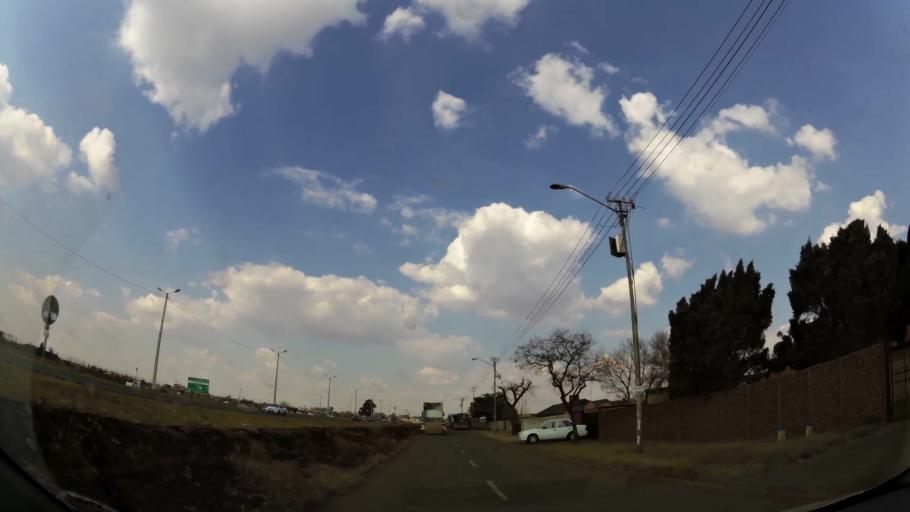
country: ZA
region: Gauteng
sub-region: Ekurhuleni Metropolitan Municipality
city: Germiston
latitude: -26.3108
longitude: 28.2011
